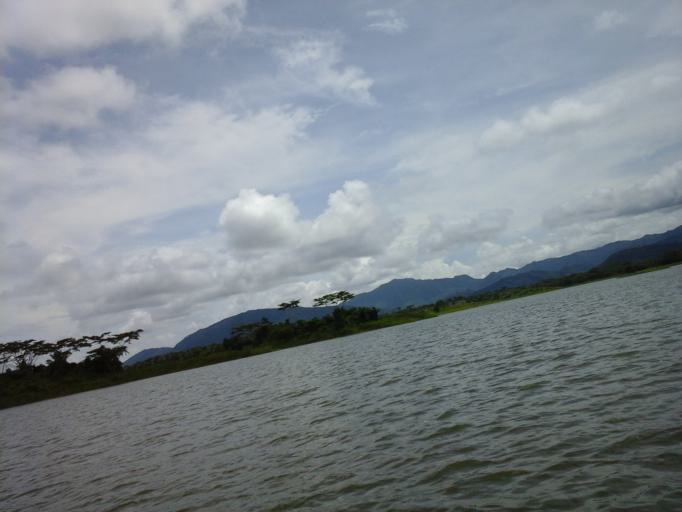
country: CO
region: Bolivar
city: San Cristobal
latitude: 9.8760
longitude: -75.3020
